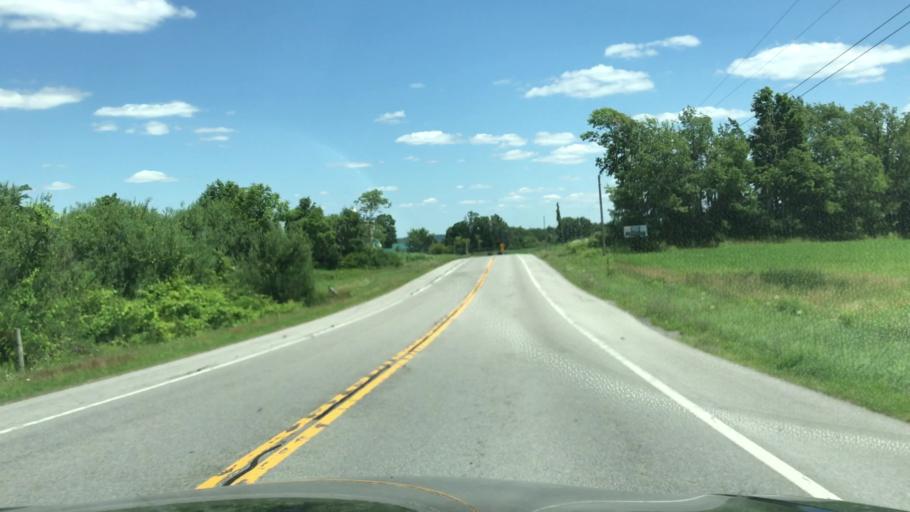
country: US
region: New York
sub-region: Wyoming County
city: Warsaw
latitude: 42.7420
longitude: -78.2057
